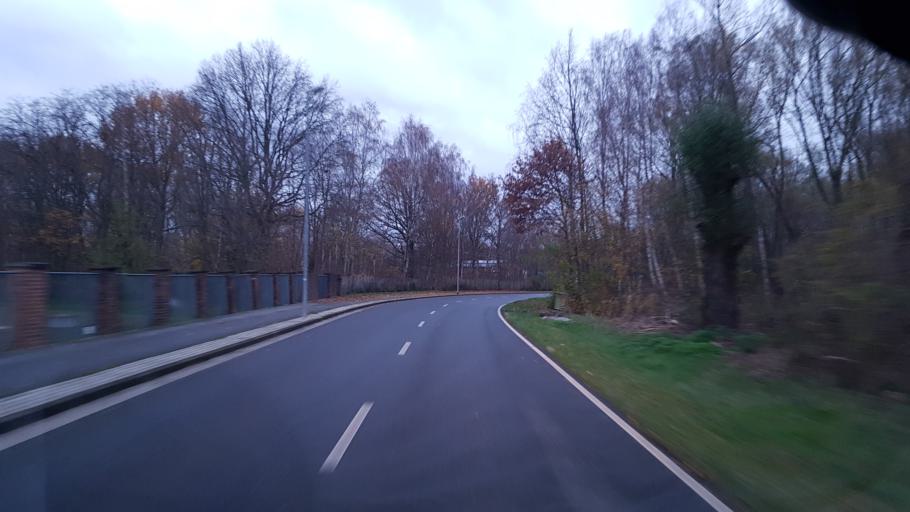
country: DE
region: Brandenburg
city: Lauchhammer
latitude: 51.4890
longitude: 13.7312
